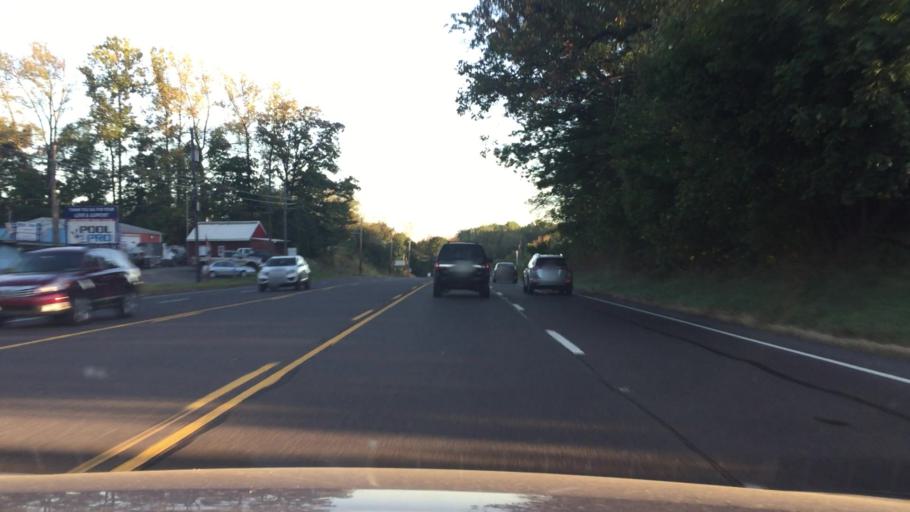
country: US
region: Pennsylvania
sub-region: Lehigh County
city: Coopersburg
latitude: 40.4903
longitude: -75.3797
